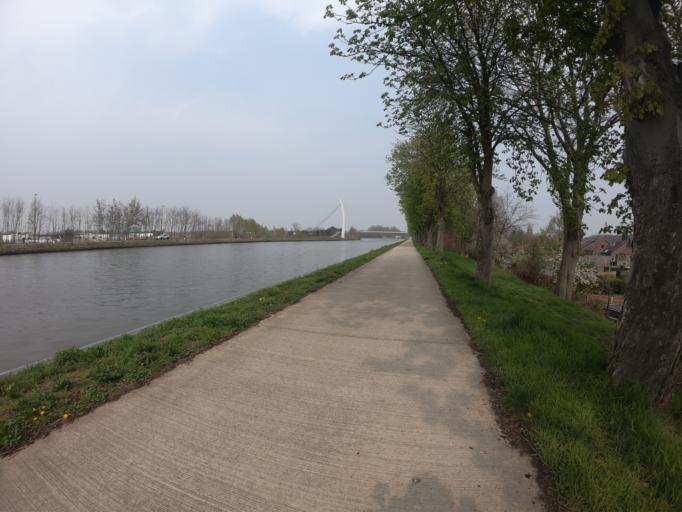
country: BE
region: Flanders
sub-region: Provincie Limburg
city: Maasmechelen
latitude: 51.0100
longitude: 5.7153
